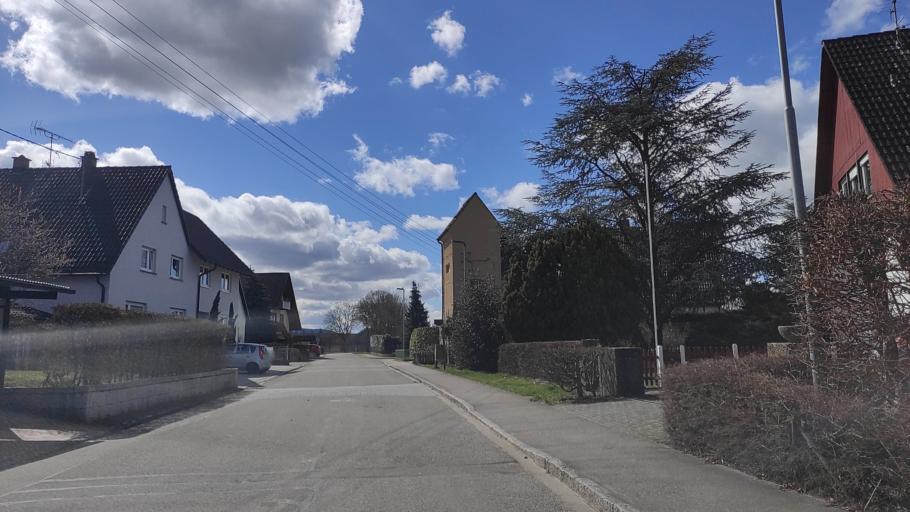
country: DE
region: Baden-Wuerttemberg
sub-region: Freiburg Region
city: Heitersheim
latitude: 47.8827
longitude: 7.6820
